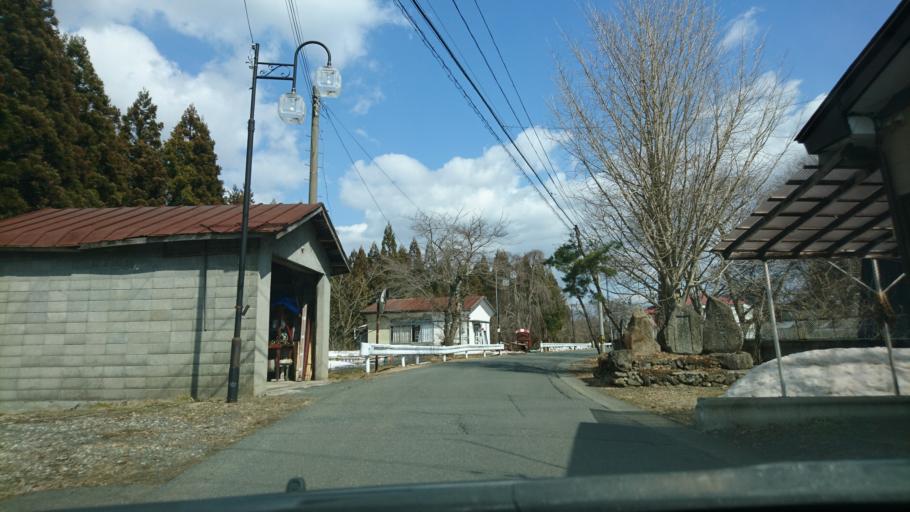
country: JP
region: Iwate
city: Shizukuishi
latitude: 39.6382
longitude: 140.9243
